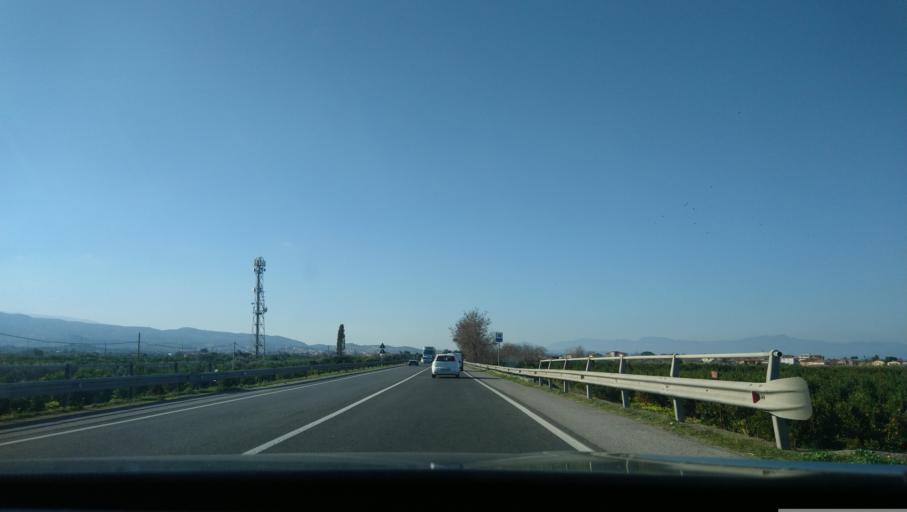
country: IT
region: Calabria
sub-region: Provincia di Cosenza
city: Fabrizio
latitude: 39.6330
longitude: 16.5586
